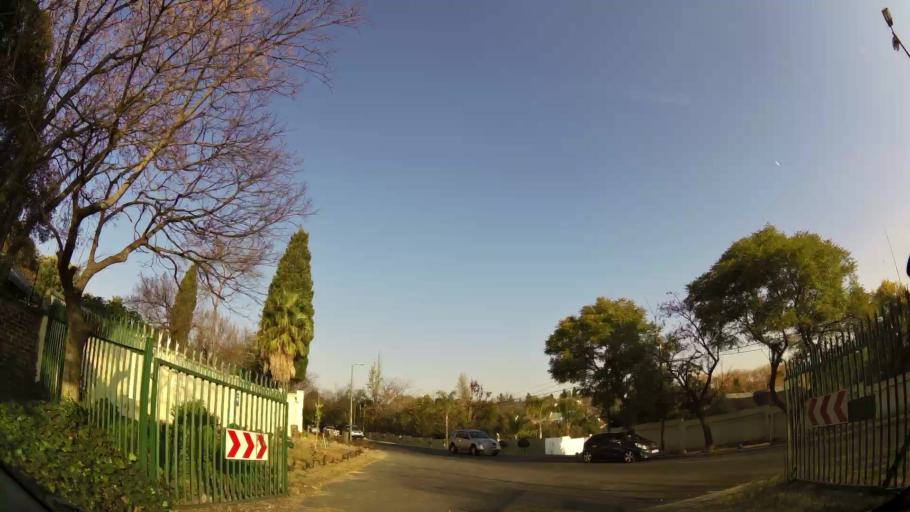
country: ZA
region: Gauteng
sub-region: City of Johannesburg Metropolitan Municipality
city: Diepsloot
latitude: -26.0631
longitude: 27.9855
